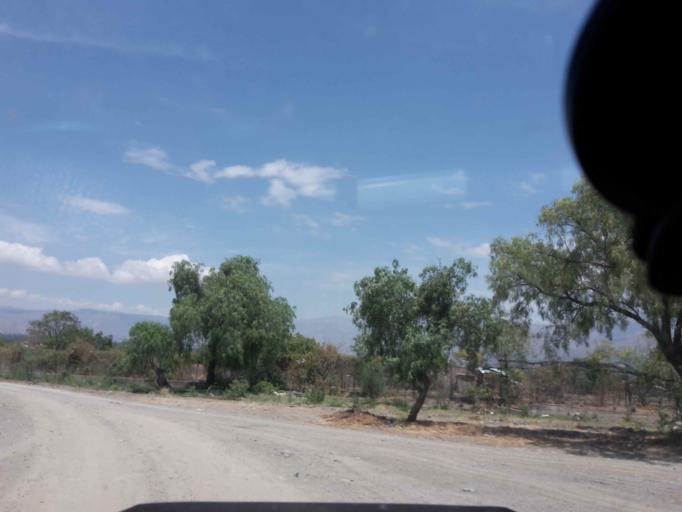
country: BO
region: Cochabamba
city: Cochabamba
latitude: -17.3312
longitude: -66.2121
